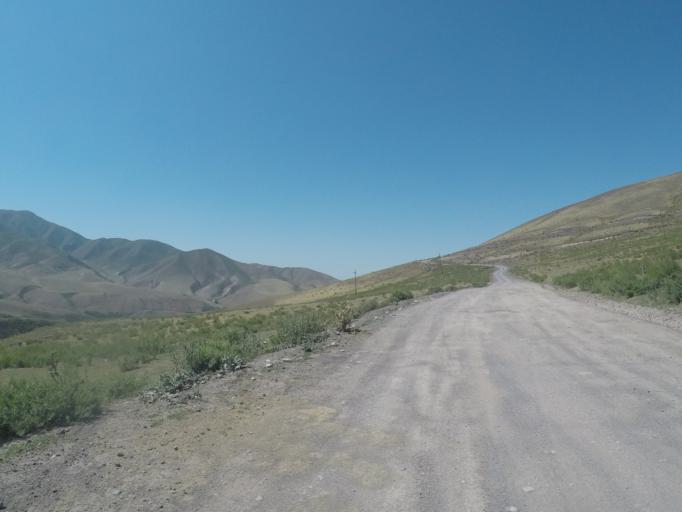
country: KG
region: Chuy
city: Bishkek
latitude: 42.6493
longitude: 74.5177
